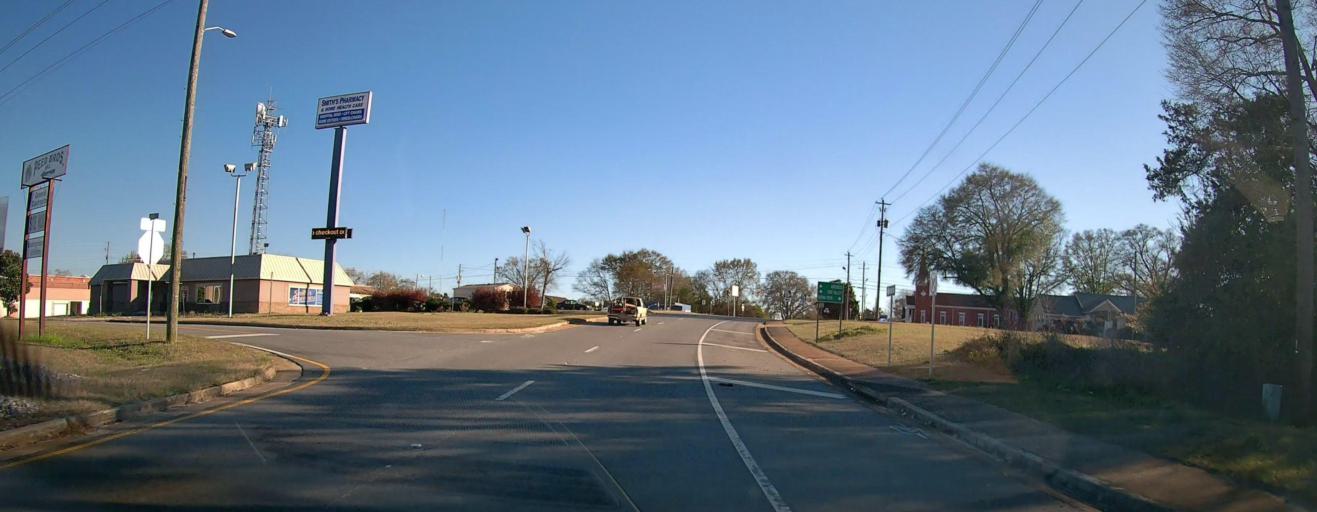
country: US
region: Georgia
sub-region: Taylor County
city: Butler
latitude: 32.5590
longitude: -84.2391
